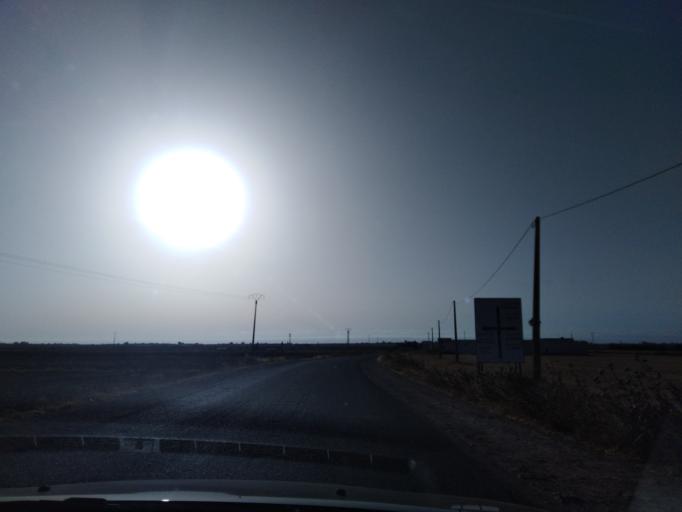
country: MA
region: Doukkala-Abda
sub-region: Safi
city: Safi
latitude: 32.4927
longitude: -8.9276
